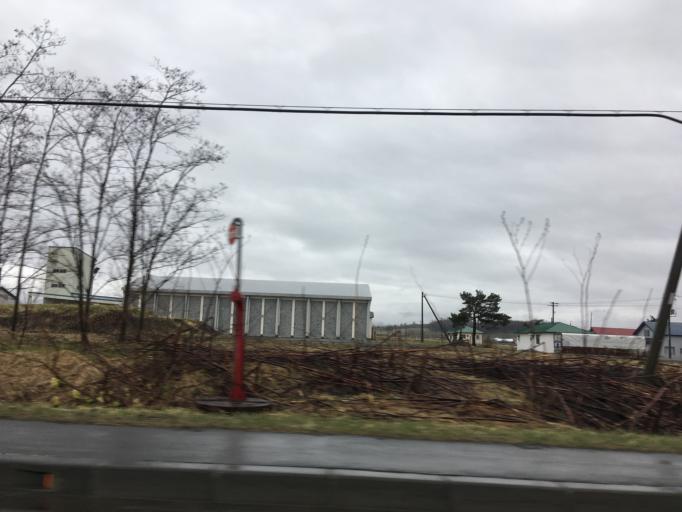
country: JP
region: Hokkaido
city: Nayoro
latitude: 44.1216
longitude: 142.4825
